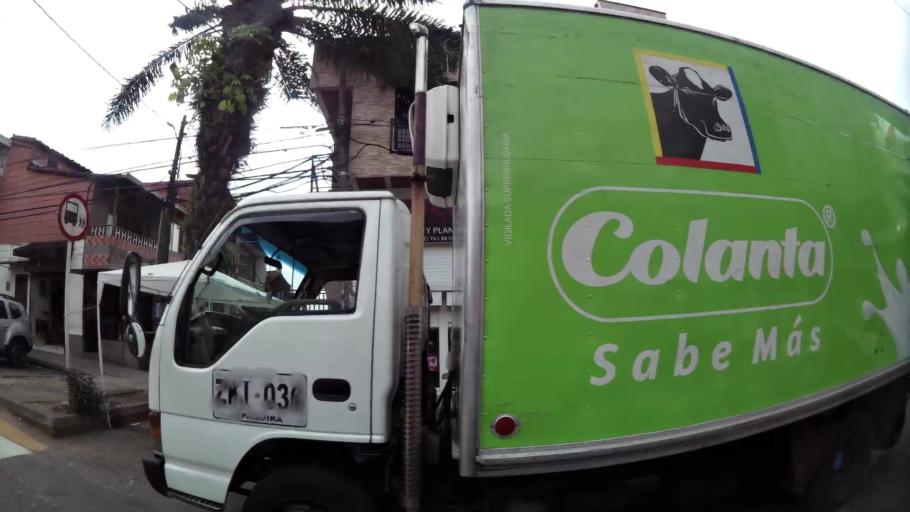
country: CO
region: Antioquia
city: Medellin
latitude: 6.2812
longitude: -75.6046
